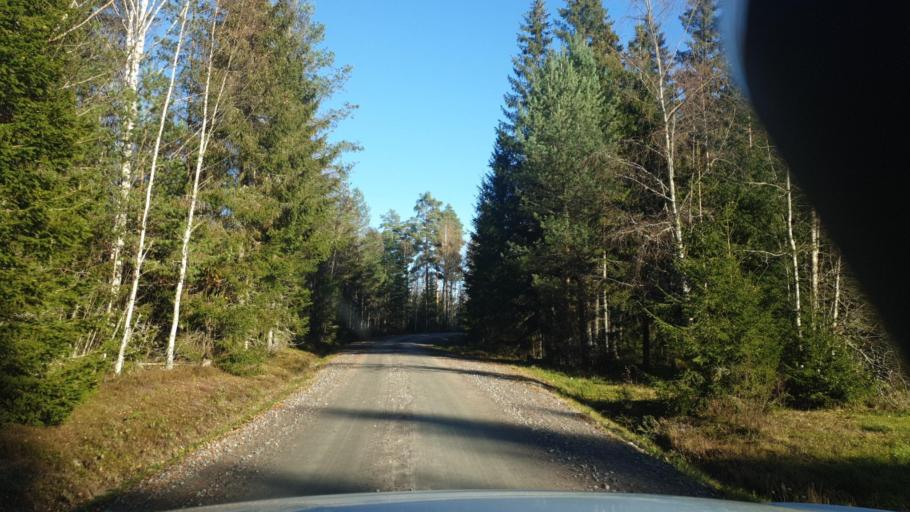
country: SE
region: Vaermland
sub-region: Karlstads Kommun
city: Edsvalla
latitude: 59.4885
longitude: 13.1642
